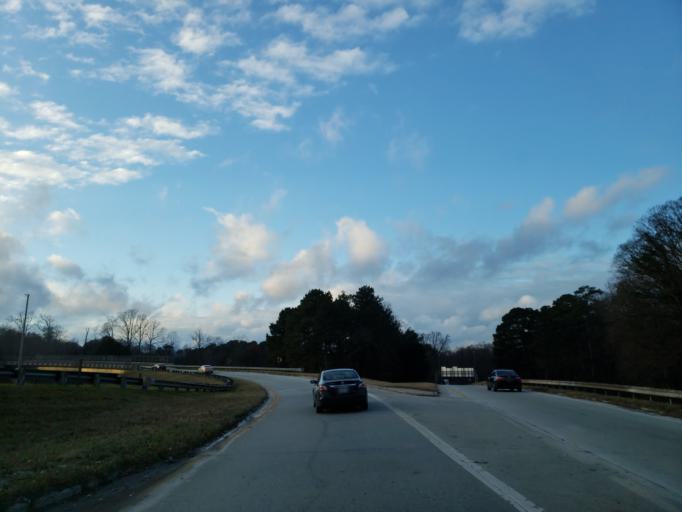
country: US
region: Georgia
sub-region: Fulton County
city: East Point
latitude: 33.6912
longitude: -84.4984
